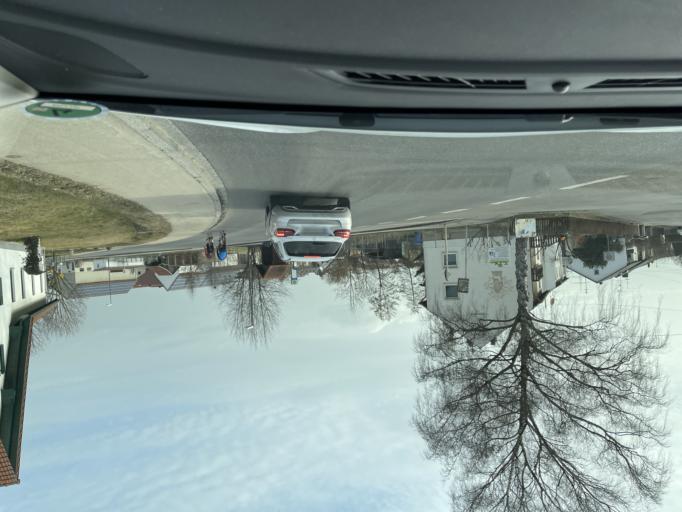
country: DE
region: Bavaria
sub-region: Swabia
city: Hollenbach
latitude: 48.4875
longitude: 11.0932
